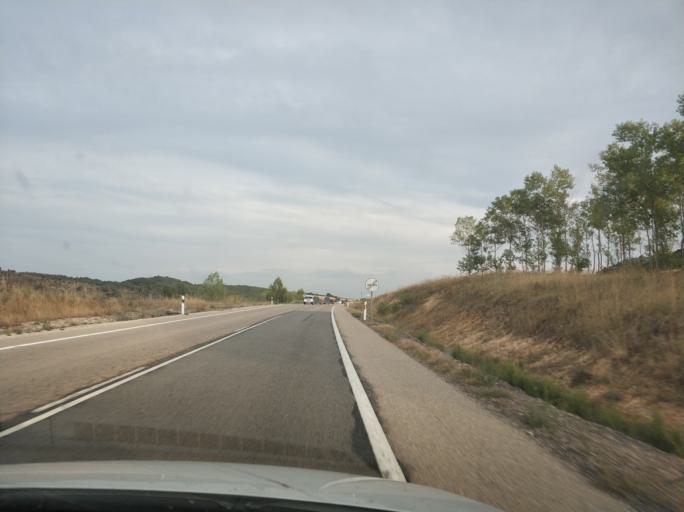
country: ES
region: Castille and Leon
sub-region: Provincia de Burgos
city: Cuevas de San Clemente
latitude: 42.1263
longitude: -3.5535
